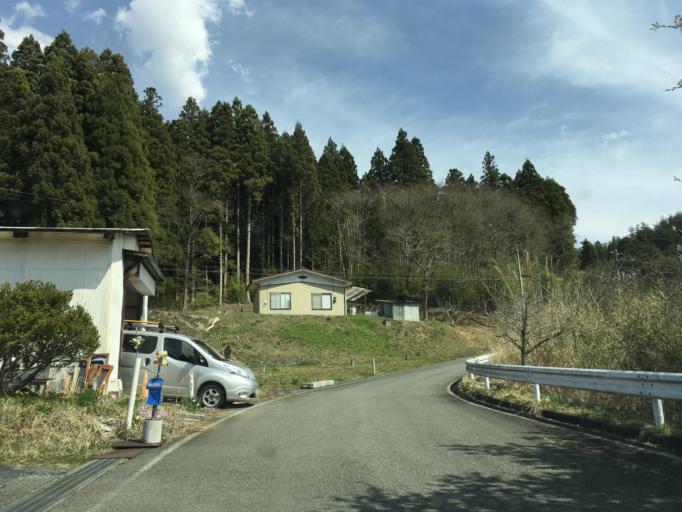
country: JP
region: Iwate
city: Ichinoseki
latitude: 38.8306
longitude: 141.3559
